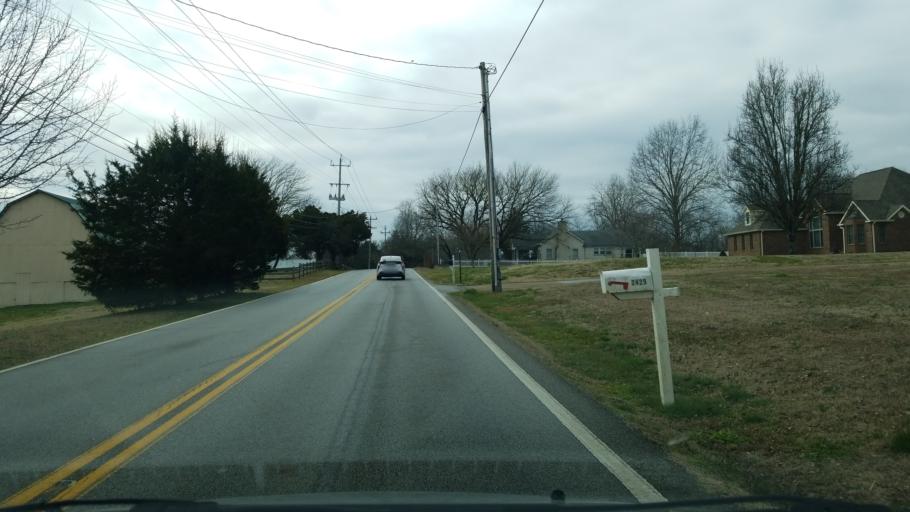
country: US
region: Tennessee
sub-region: Hamilton County
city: Collegedale
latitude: 35.0198
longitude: -85.0870
